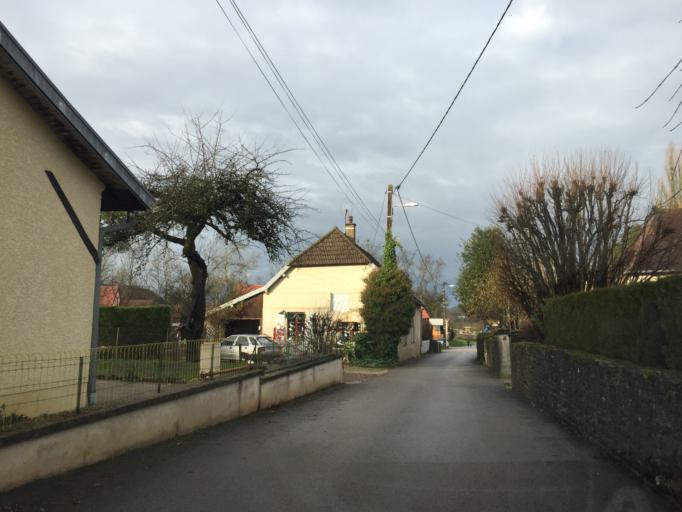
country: FR
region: Franche-Comte
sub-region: Departement du Jura
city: Mont-sous-Vaudrey
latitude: 46.9799
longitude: 5.6002
